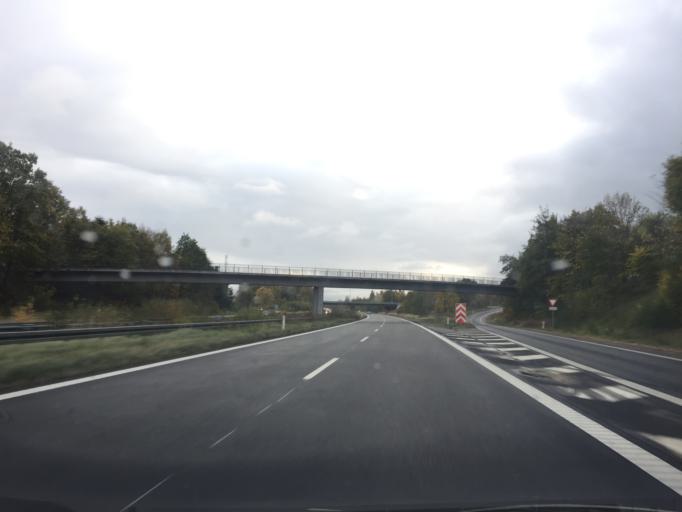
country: DK
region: Capital Region
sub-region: Fredensborg Kommune
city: Kokkedal
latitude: 55.9117
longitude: 12.4711
